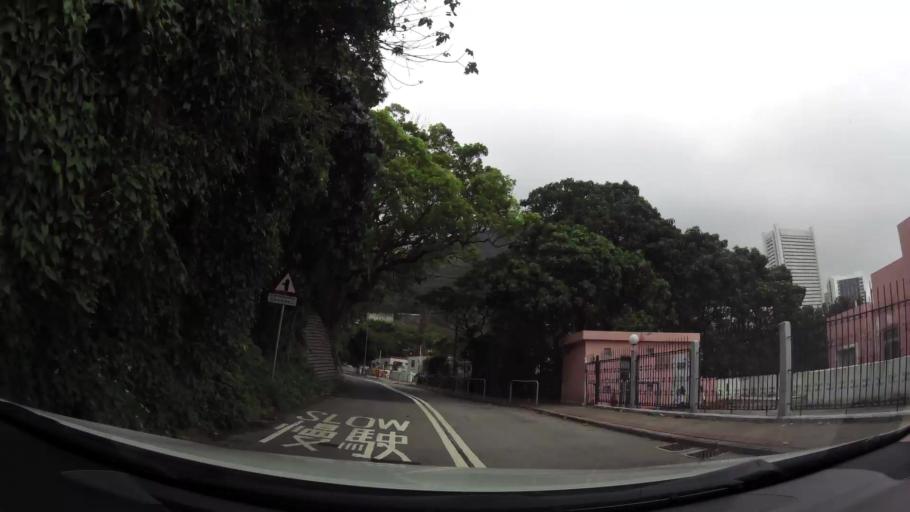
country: HK
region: Central and Western
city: Central
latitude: 22.2745
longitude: 114.1275
